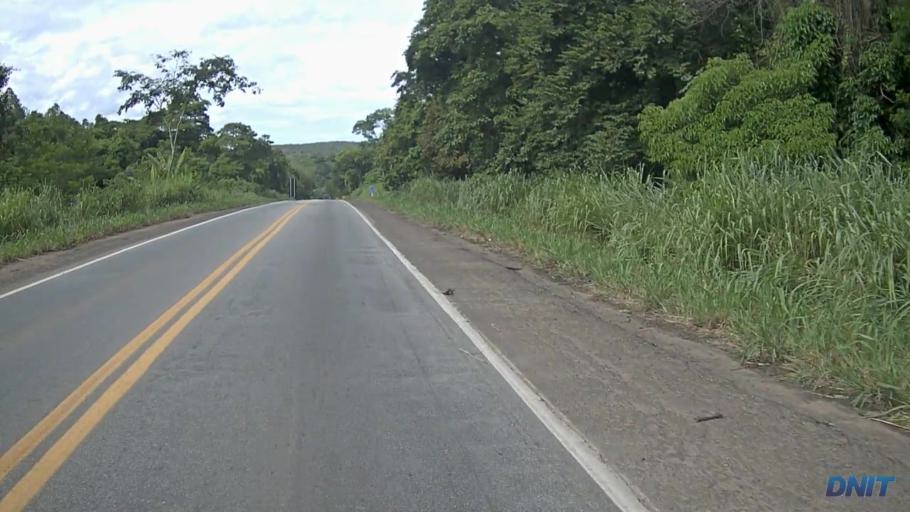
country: BR
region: Minas Gerais
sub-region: Ipaba
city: Ipaba
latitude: -19.3409
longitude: -42.4296
